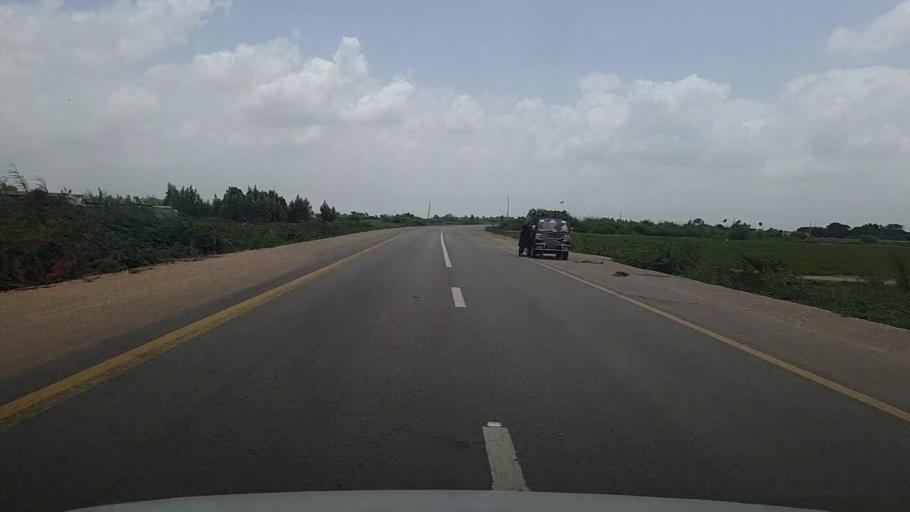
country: PK
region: Sindh
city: Thatta
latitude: 24.7531
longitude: 67.9528
